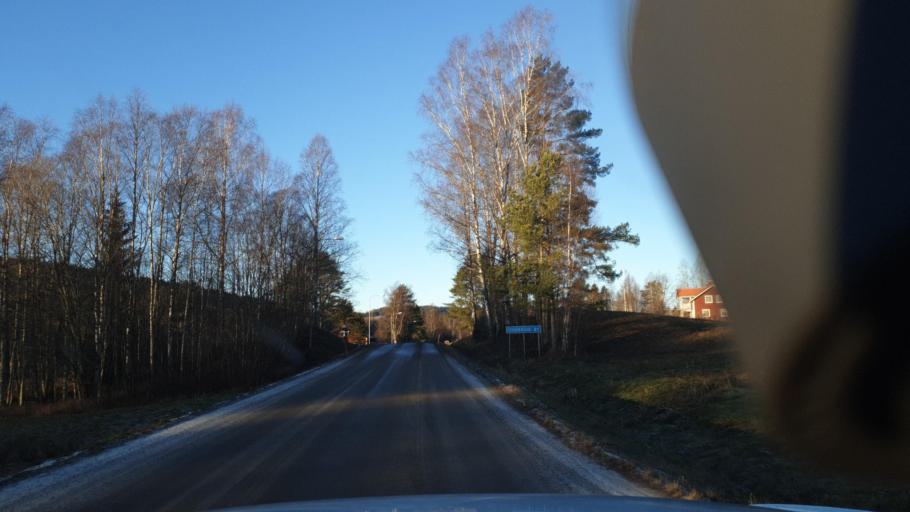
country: SE
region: Vaermland
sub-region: Arvika Kommun
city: Arvika
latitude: 59.7438
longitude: 12.8095
